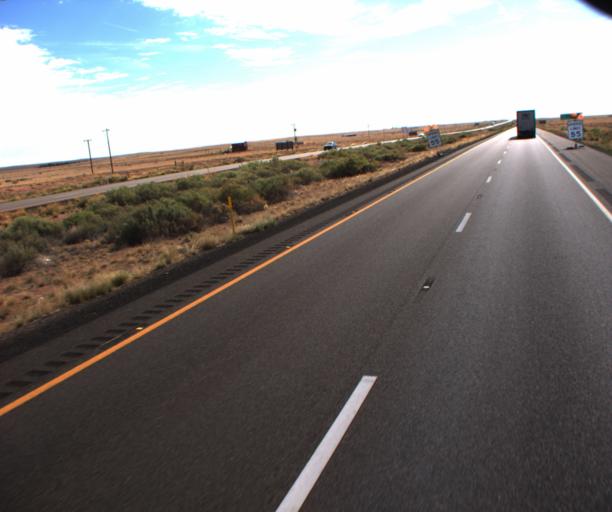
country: US
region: Arizona
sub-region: Navajo County
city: Holbrook
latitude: 34.9830
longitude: -110.0407
